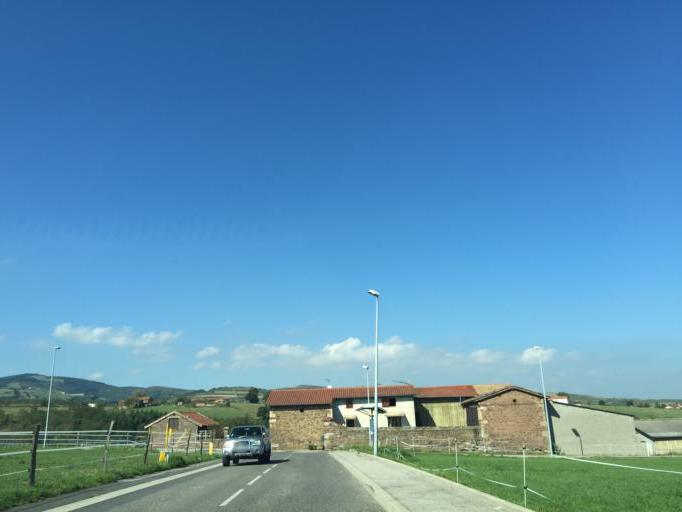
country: FR
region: Rhone-Alpes
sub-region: Departement de la Loire
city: La Grand-Croix
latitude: 45.4919
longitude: 4.5409
